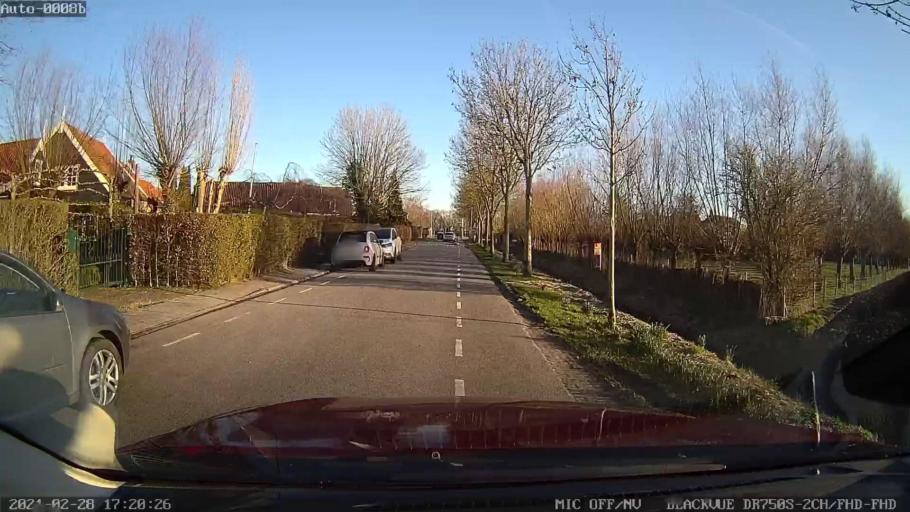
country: NL
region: Zeeland
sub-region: Schouwen-Duiveland
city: Bruinisse
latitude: 51.6896
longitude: 3.9792
